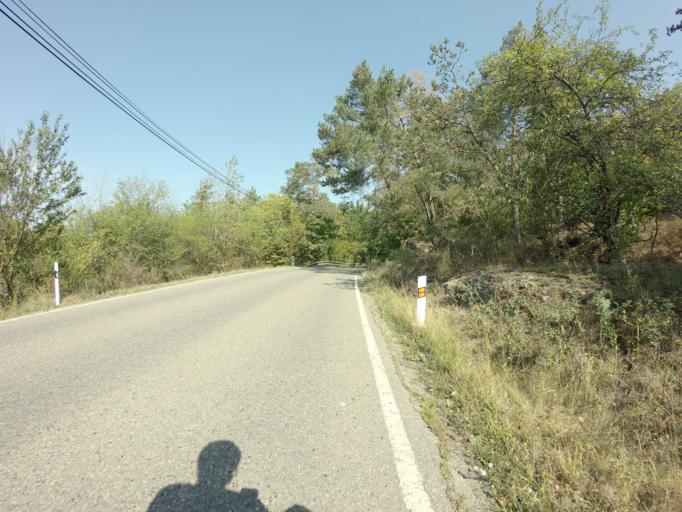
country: CZ
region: Central Bohemia
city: Kamenny Privoz
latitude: 49.8593
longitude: 14.5419
